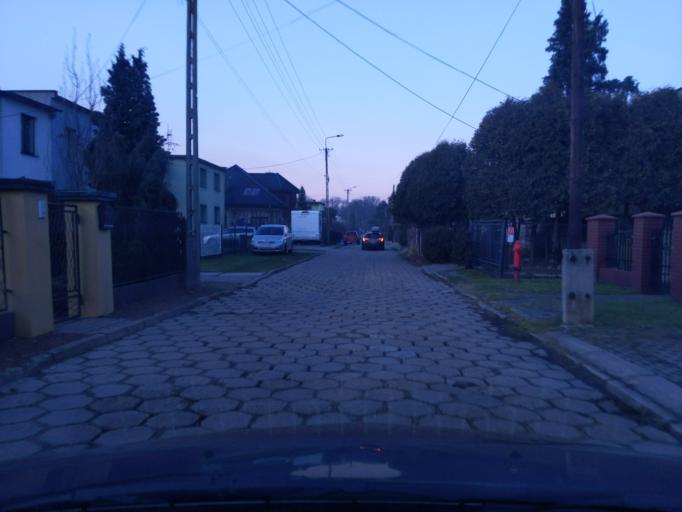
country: PL
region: Silesian Voivodeship
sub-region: Powiat pszczynski
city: Pszczyna
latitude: 49.9693
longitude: 18.9357
